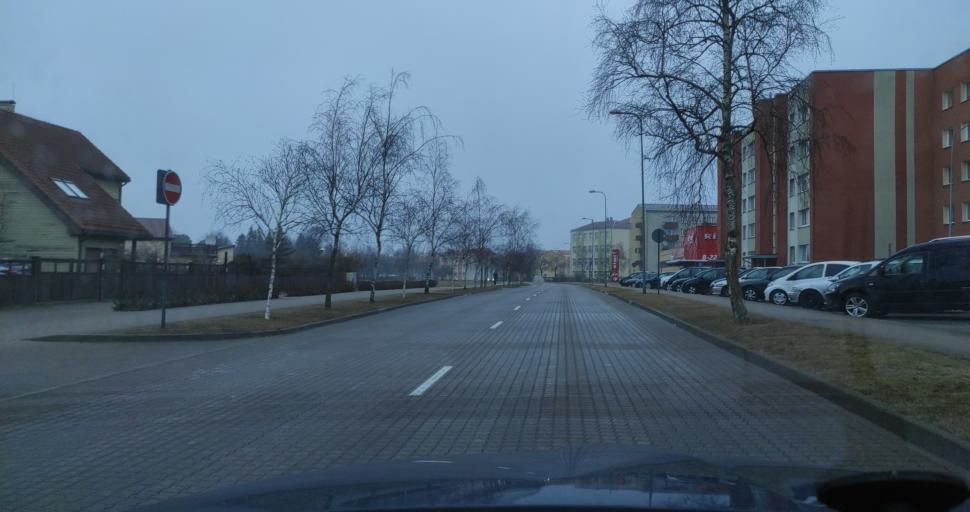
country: LV
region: Ventspils
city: Ventspils
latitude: 57.3861
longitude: 21.5475
